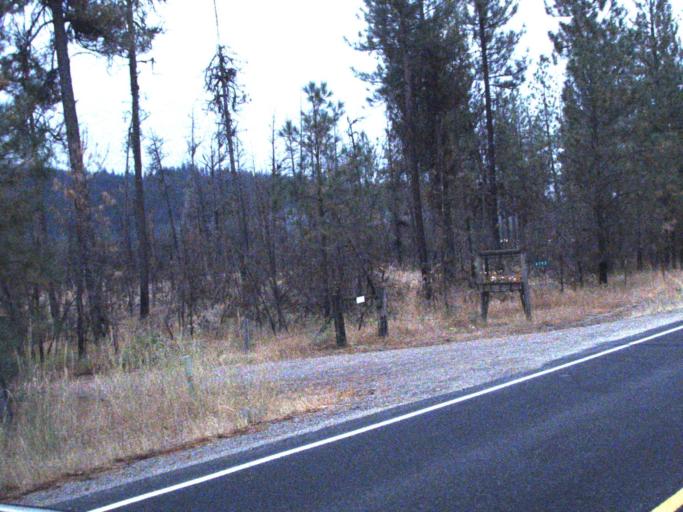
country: US
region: Washington
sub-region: Spokane County
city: Deer Park
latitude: 47.9584
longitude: -117.7511
